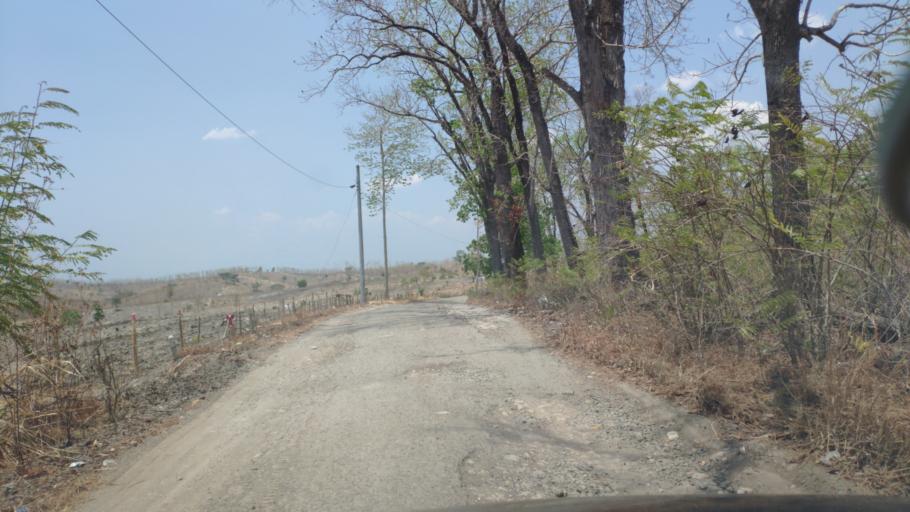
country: ID
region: Central Java
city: Temulus
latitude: -7.2755
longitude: 111.3785
